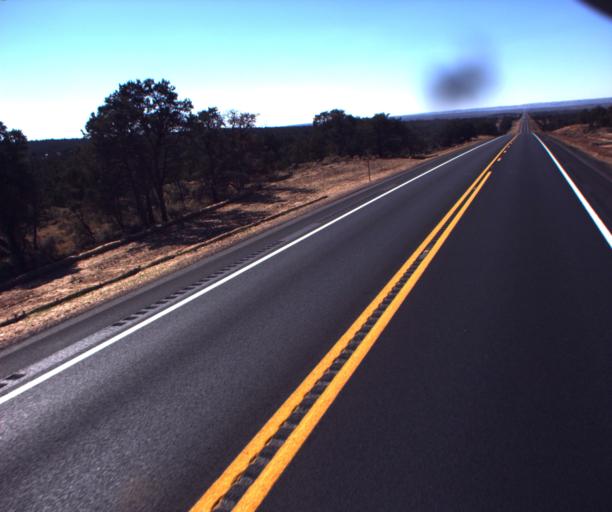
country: US
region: Arizona
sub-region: Apache County
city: Ganado
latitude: 35.7192
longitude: -109.3770
